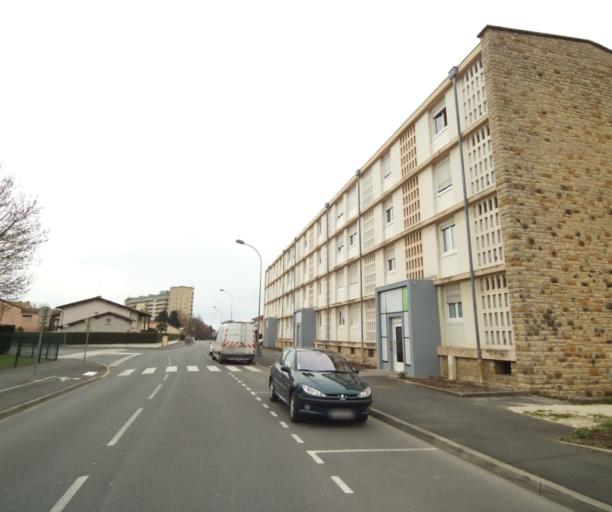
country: FR
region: Bourgogne
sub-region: Departement de Saone-et-Loire
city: Macon
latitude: 46.3052
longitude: 4.8134
